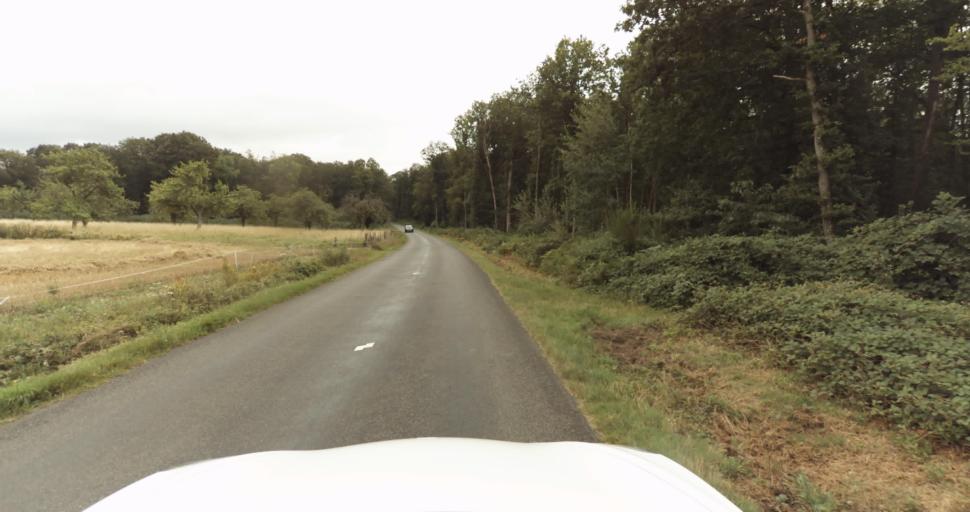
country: FR
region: Haute-Normandie
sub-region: Departement de l'Eure
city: Arnieres-sur-Iton
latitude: 48.9524
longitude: 1.0684
